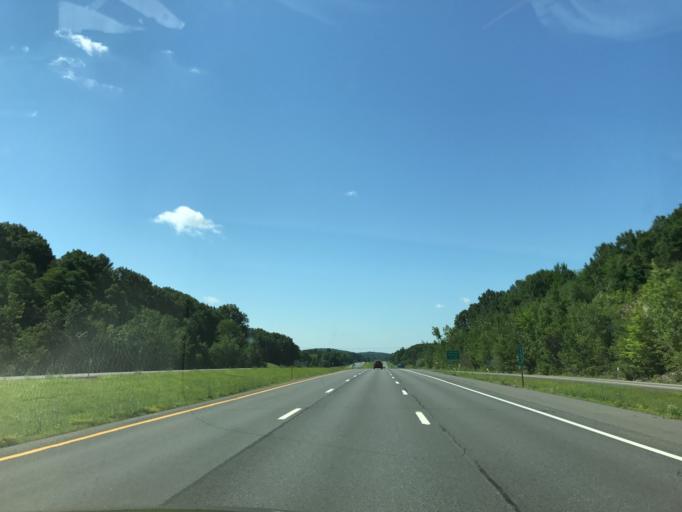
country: US
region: New York
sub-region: Rensselaer County
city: East Greenbush
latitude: 42.5779
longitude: -73.6793
